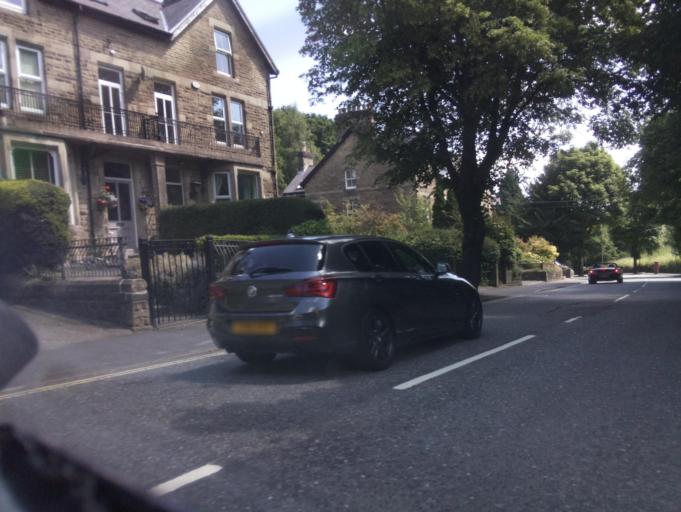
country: GB
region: England
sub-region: Derbyshire
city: Buxton
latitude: 53.2539
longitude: -1.9065
